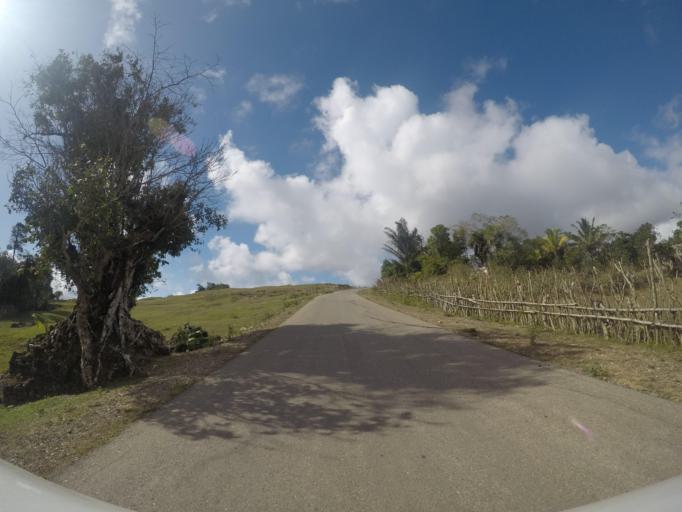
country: TL
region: Lautem
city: Lospalos
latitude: -8.4801
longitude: 126.8694
